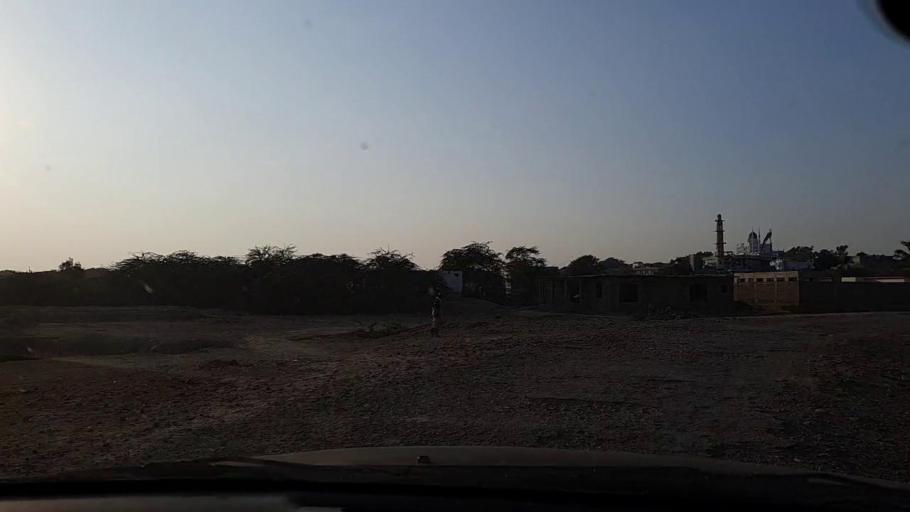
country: PK
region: Sindh
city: Thatta
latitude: 24.5574
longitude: 67.8821
